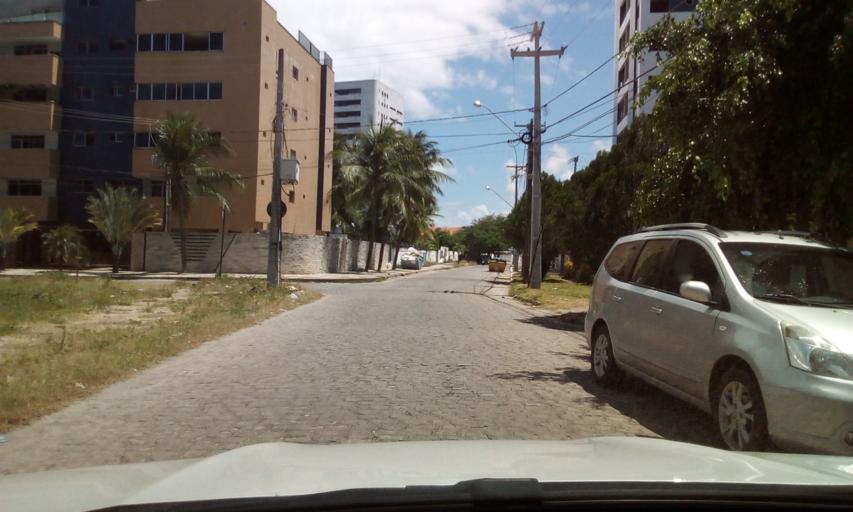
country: BR
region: Paraiba
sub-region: Joao Pessoa
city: Joao Pessoa
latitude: -7.0774
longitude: -34.8324
